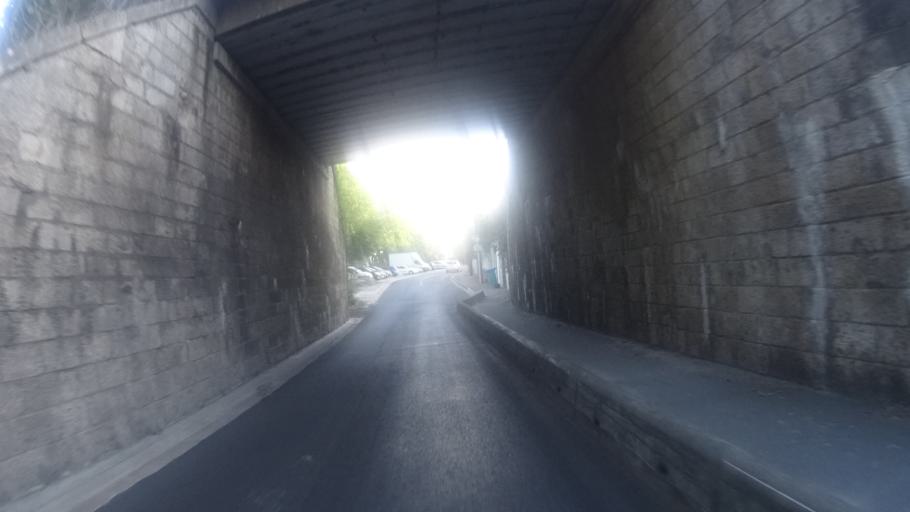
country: FR
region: Ile-de-France
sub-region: Departement de l'Essonne
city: Ormoy
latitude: 48.5807
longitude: 2.4709
